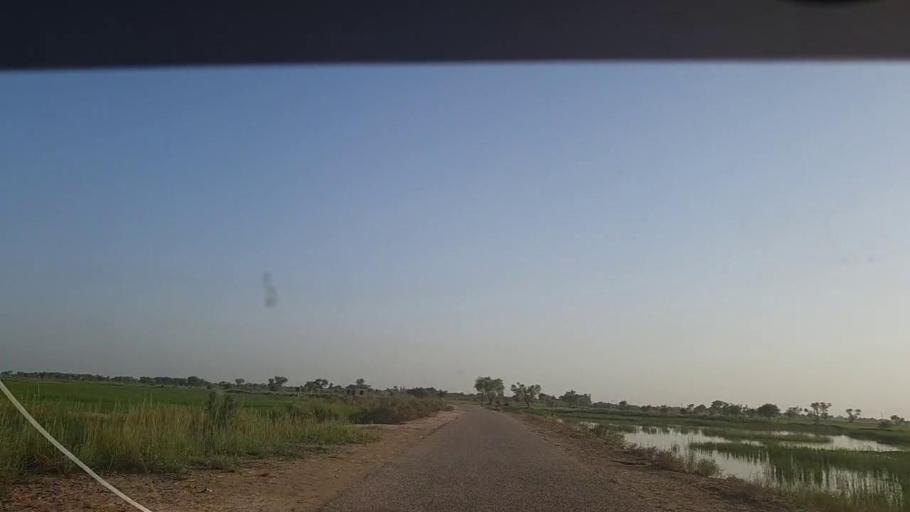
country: PK
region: Sindh
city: Thul
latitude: 28.1917
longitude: 68.8722
